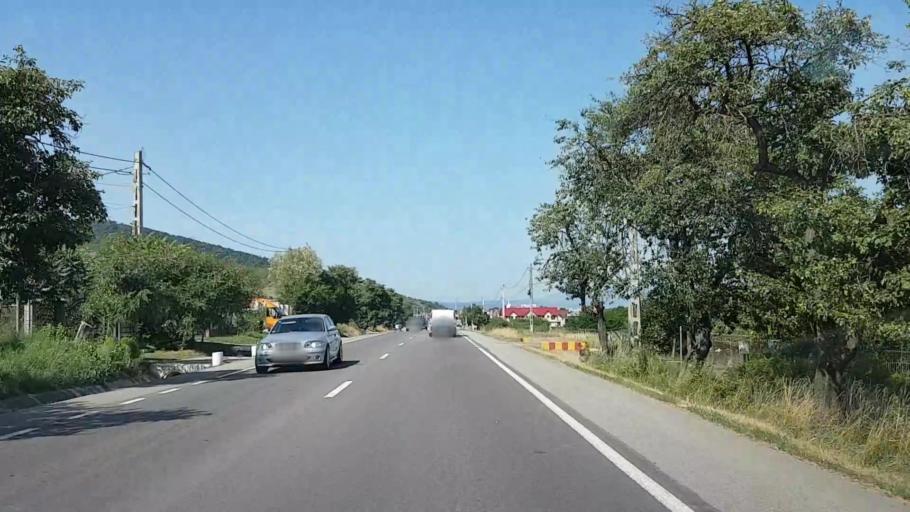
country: RO
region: Bistrita-Nasaud
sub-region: Municipiul Bistrita
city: Viisoara
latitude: 47.0927
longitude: 24.4360
